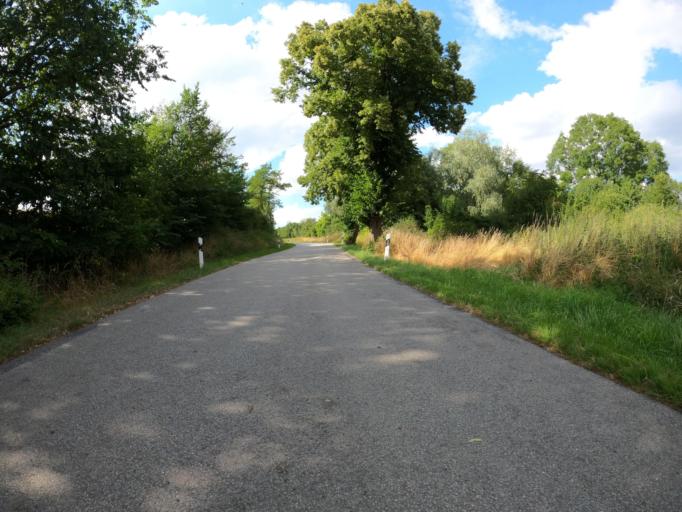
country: DE
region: Mecklenburg-Vorpommern
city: Woldegk
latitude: 53.4422
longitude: 13.5905
